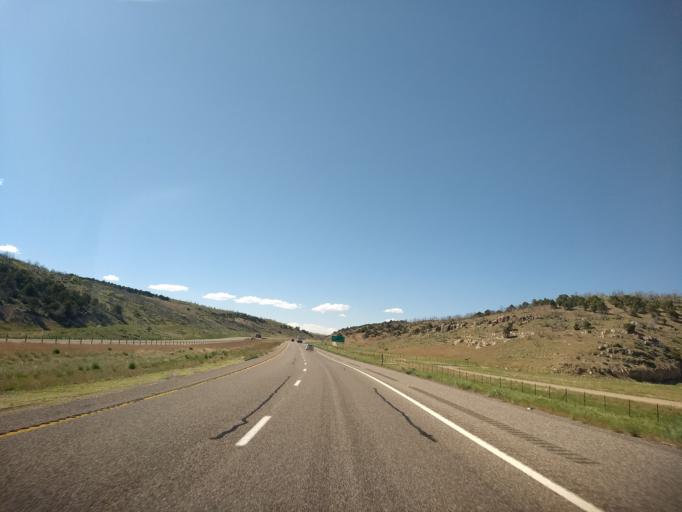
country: US
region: Utah
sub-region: Millard County
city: Fillmore
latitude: 38.6738
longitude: -112.5900
